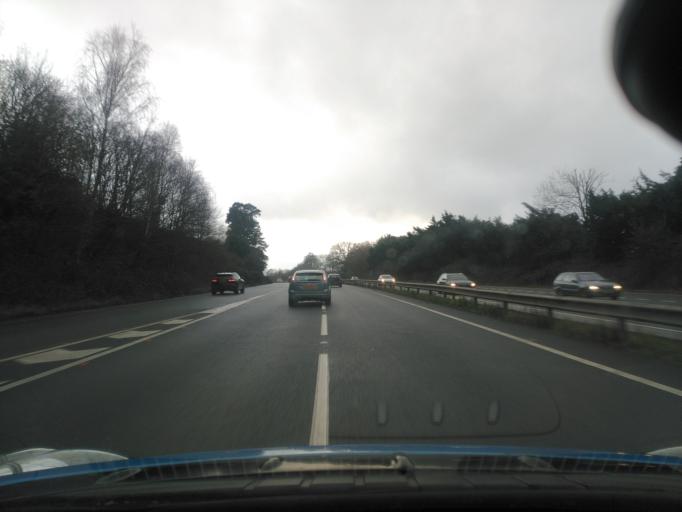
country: GB
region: England
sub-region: Surrey
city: Godalming
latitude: 51.2153
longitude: -0.6459
